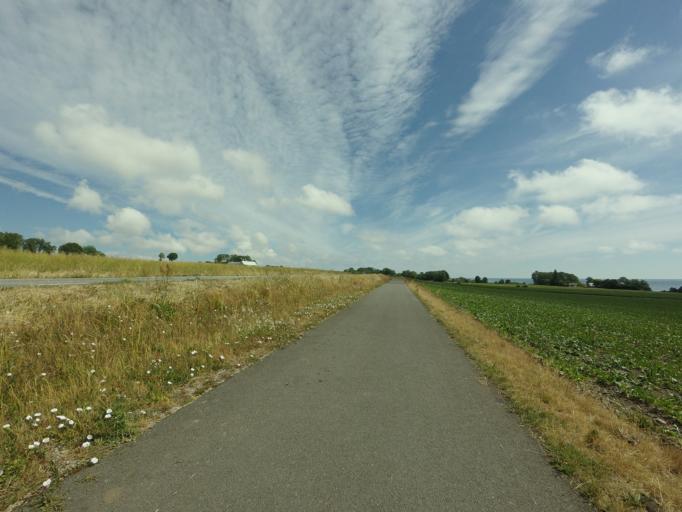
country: SE
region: Skane
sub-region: Simrishamns Kommun
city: Simrishamn
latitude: 55.4922
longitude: 14.3116
